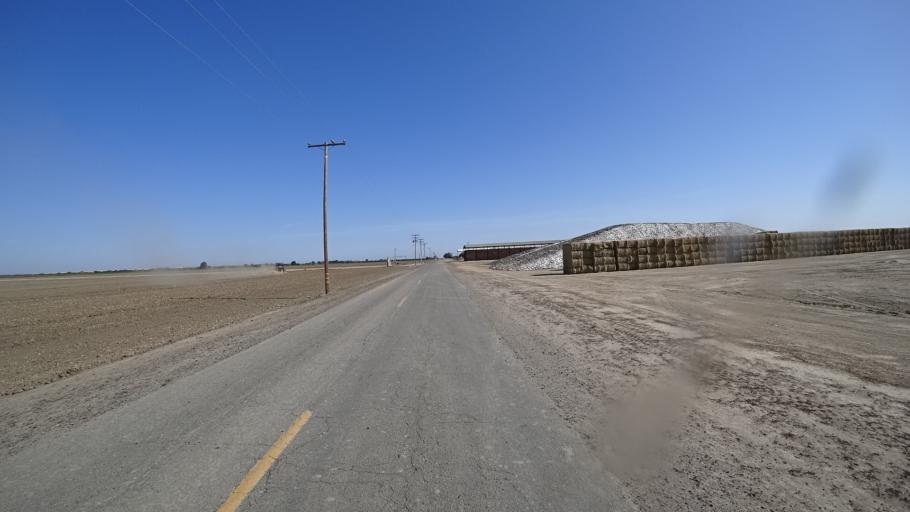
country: US
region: California
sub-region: Kings County
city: Home Garden
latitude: 36.2384
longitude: -119.5562
